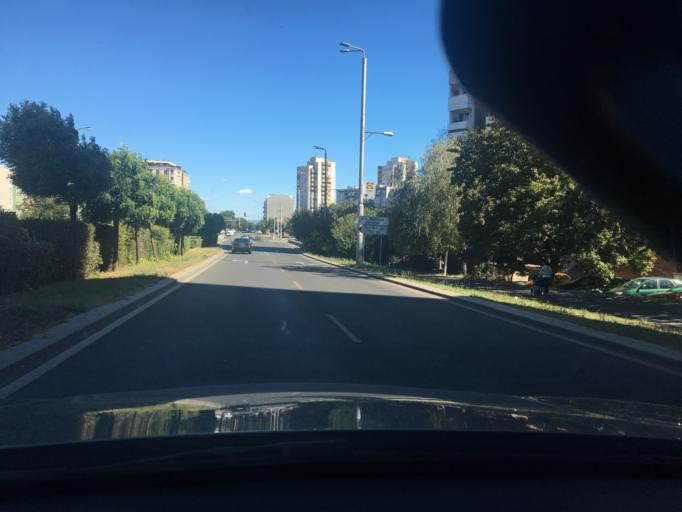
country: BG
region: Burgas
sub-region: Obshtina Burgas
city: Burgas
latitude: 42.5199
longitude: 27.4640
